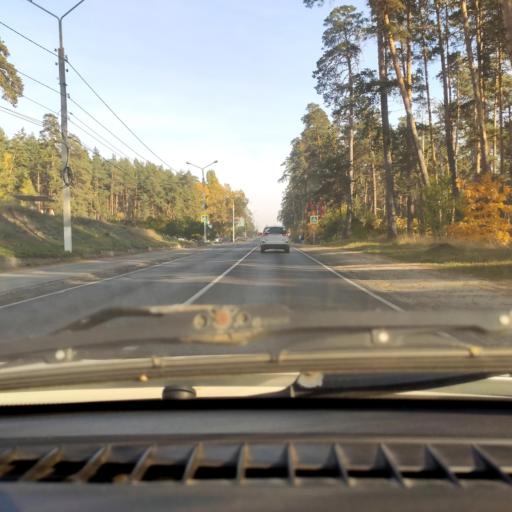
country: RU
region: Samara
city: Tol'yatti
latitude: 53.4758
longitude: 49.3375
